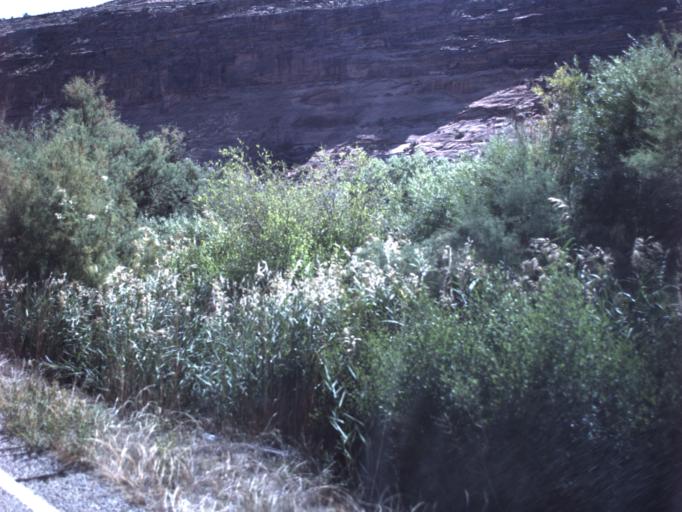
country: US
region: Utah
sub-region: Grand County
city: Moab
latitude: 38.5385
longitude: -109.6303
